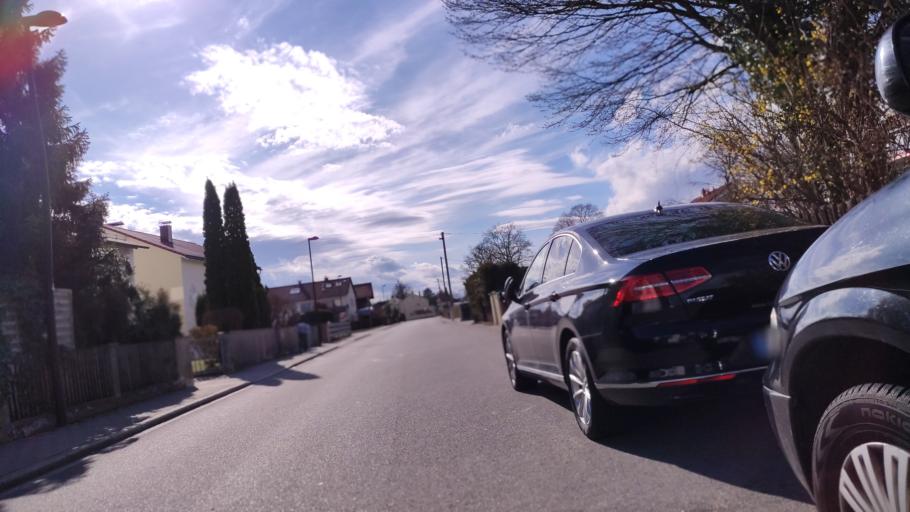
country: DE
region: Bavaria
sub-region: Upper Bavaria
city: Emmering
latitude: 48.1870
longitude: 11.2773
